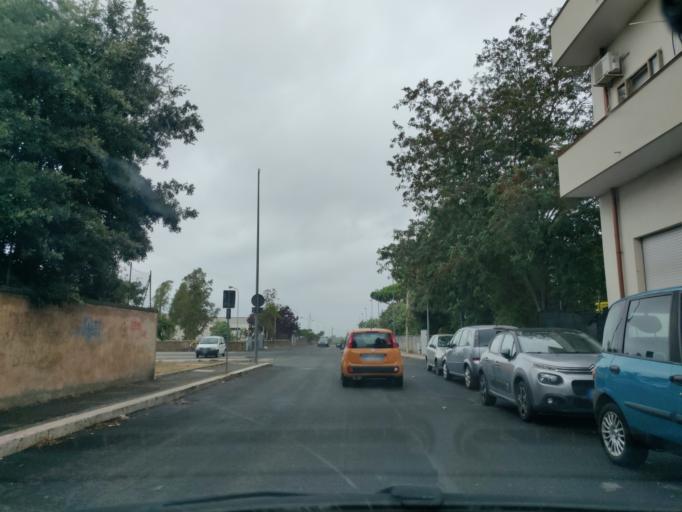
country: IT
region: Latium
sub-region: Citta metropolitana di Roma Capitale
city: Civitavecchia
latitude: 42.1023
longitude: 11.7981
